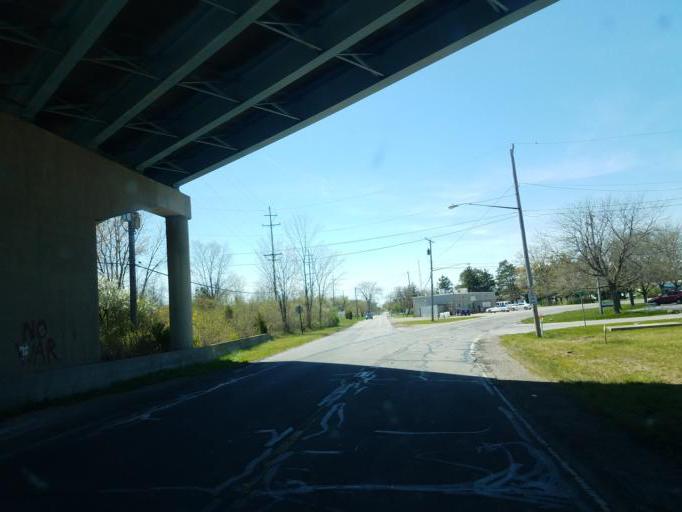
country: US
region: Ohio
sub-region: Ottawa County
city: Port Clinton
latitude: 41.5087
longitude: -82.9110
